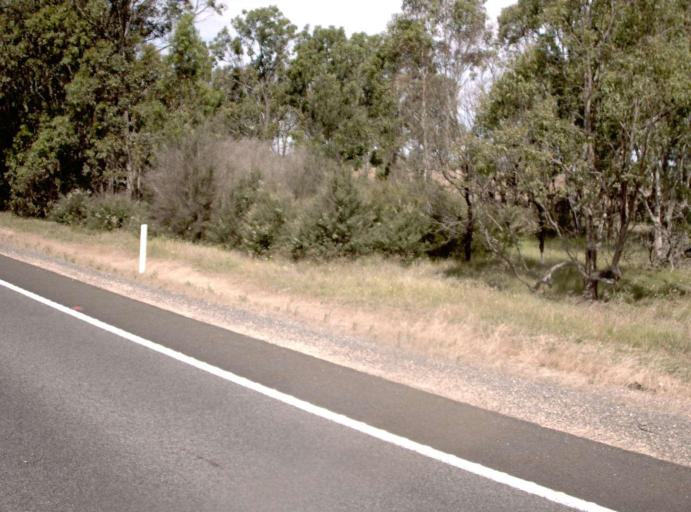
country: AU
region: Victoria
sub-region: East Gippsland
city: Bairnsdale
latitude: -37.8719
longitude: 147.4640
